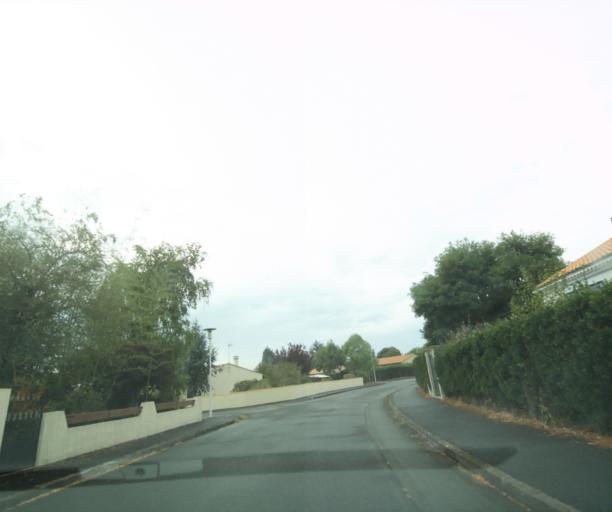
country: FR
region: Poitou-Charentes
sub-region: Departement de la Charente-Maritime
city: Tonnay-Charente
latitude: 45.9492
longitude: -0.9316
